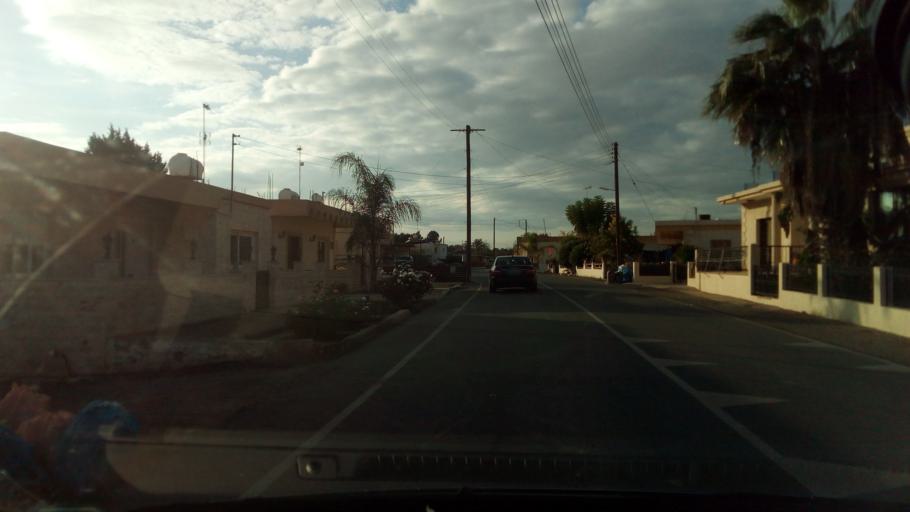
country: CY
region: Larnaka
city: Xylotymbou
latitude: 34.9955
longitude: 33.7702
